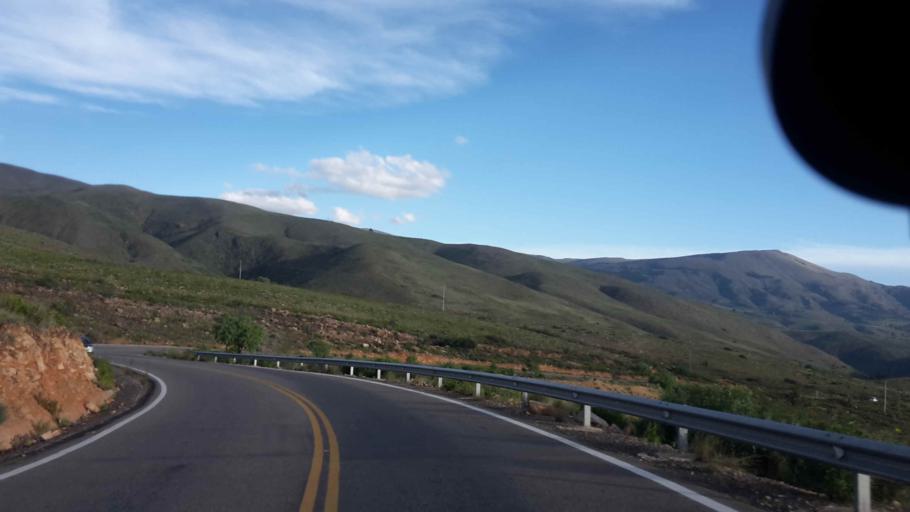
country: BO
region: Cochabamba
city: Arani
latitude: -17.5763
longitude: -65.7403
